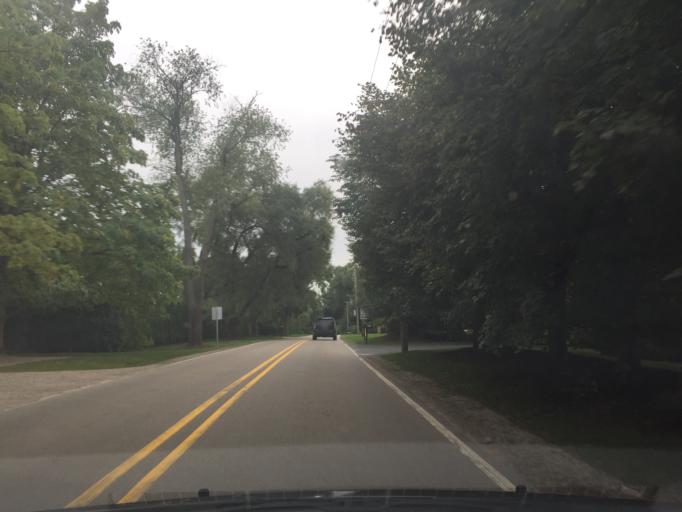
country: US
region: Michigan
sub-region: Oakland County
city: Bloomfield Hills
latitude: 42.5729
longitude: -83.2595
